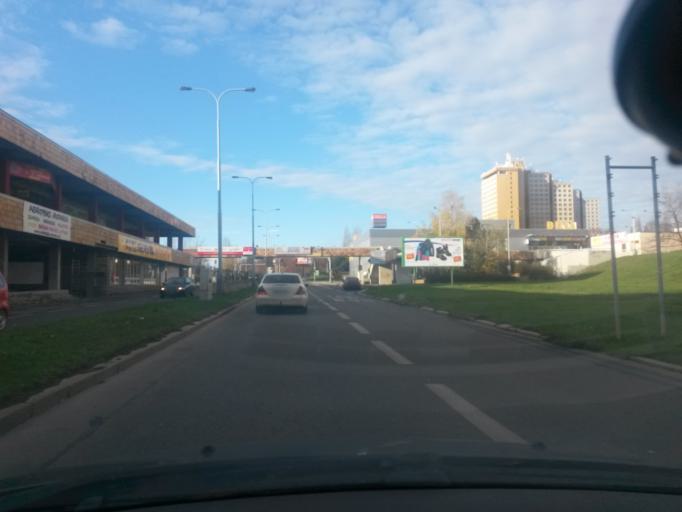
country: CZ
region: Central Bohemia
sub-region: Okres Praha-Zapad
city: Pruhonice
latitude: 50.0255
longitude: 14.5169
